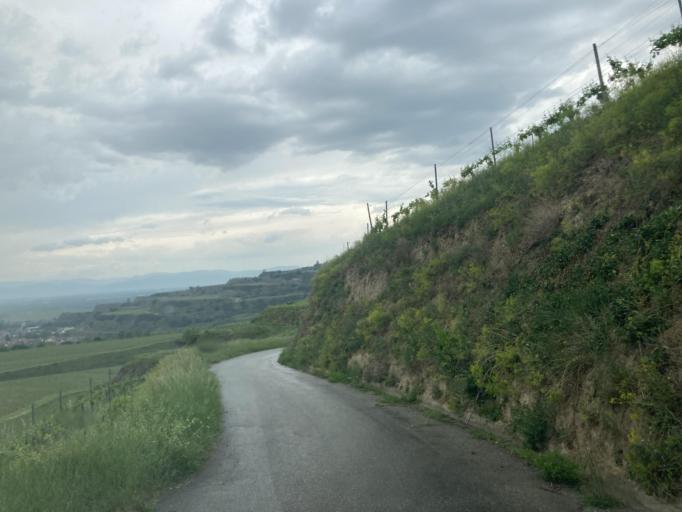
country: DE
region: Baden-Wuerttemberg
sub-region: Freiburg Region
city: Vogtsburg
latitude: 48.0888
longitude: 7.6537
